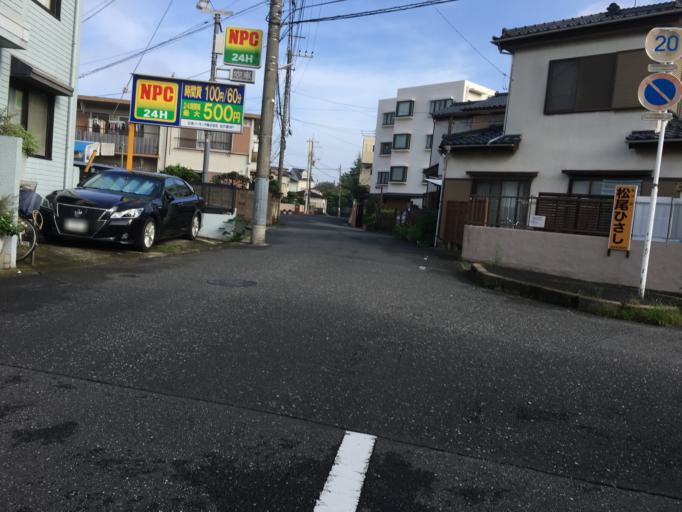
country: JP
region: Chiba
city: Matsudo
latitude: 35.7905
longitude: 139.8997
